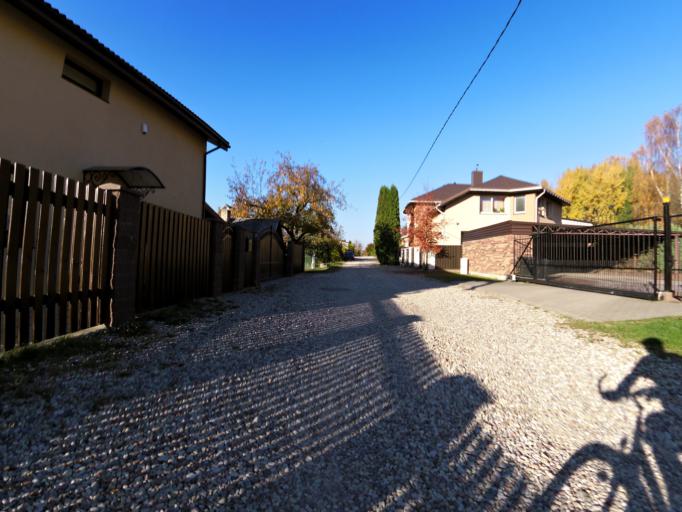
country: LT
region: Vilnius County
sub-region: Vilnius
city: Fabijoniskes
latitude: 54.7418
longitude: 25.2598
